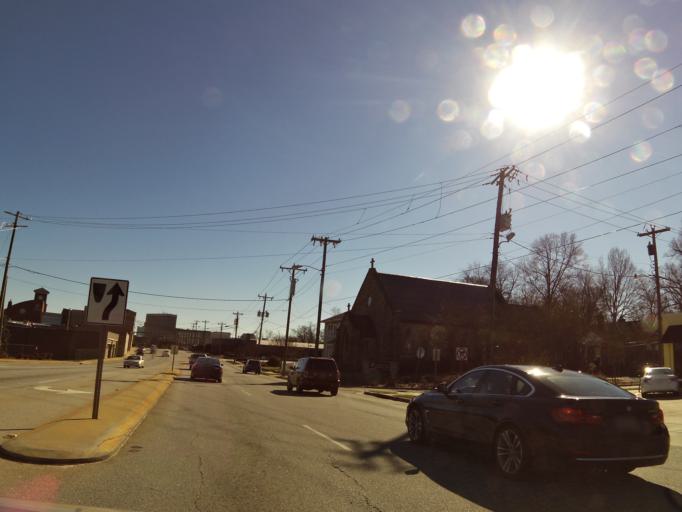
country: US
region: South Carolina
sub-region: Greenville County
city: Greenville
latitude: 34.8588
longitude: -82.4049
